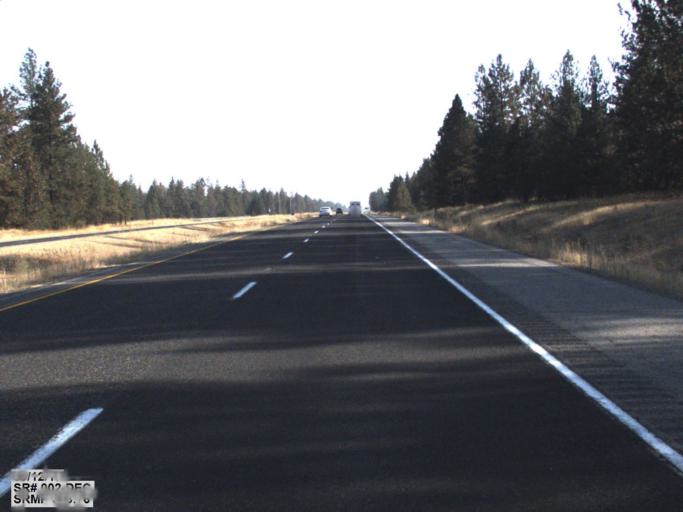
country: US
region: Washington
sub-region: Spokane County
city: Mead
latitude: 47.8793
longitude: -117.3579
